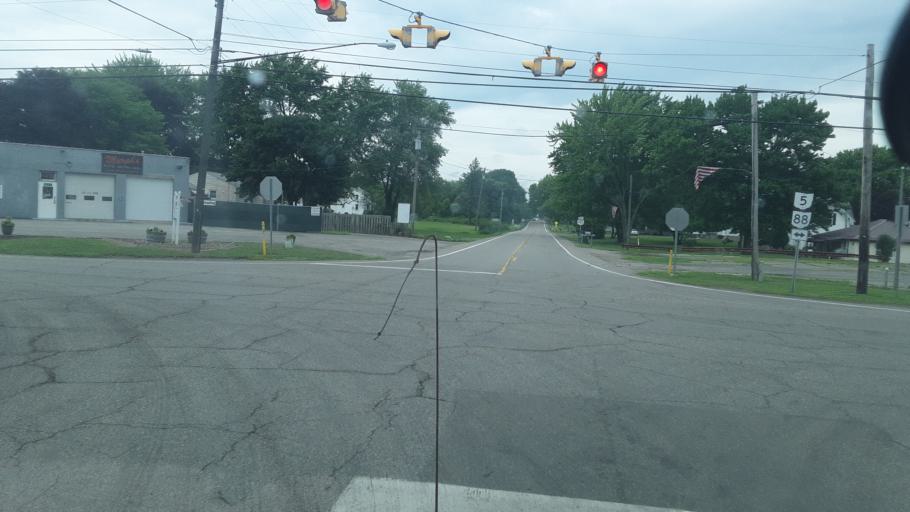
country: US
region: Ohio
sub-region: Trumbull County
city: Cortland
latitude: 41.3887
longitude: -80.6655
